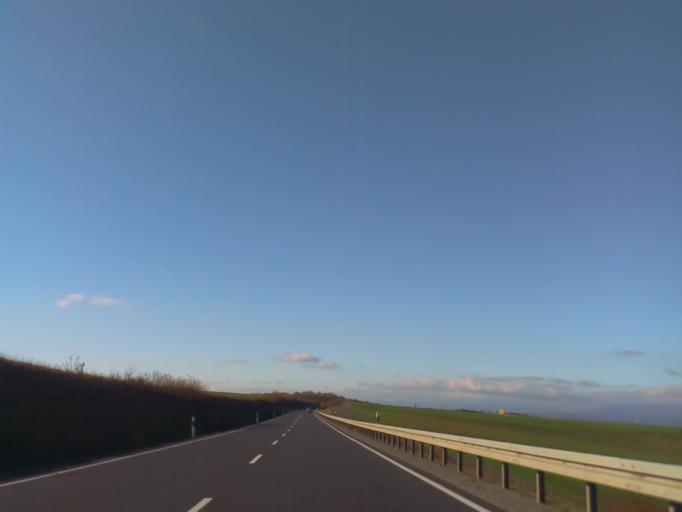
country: DE
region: Bavaria
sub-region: Regierungsbezirk Unterfranken
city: Rodelmaier
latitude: 50.3301
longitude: 10.2813
